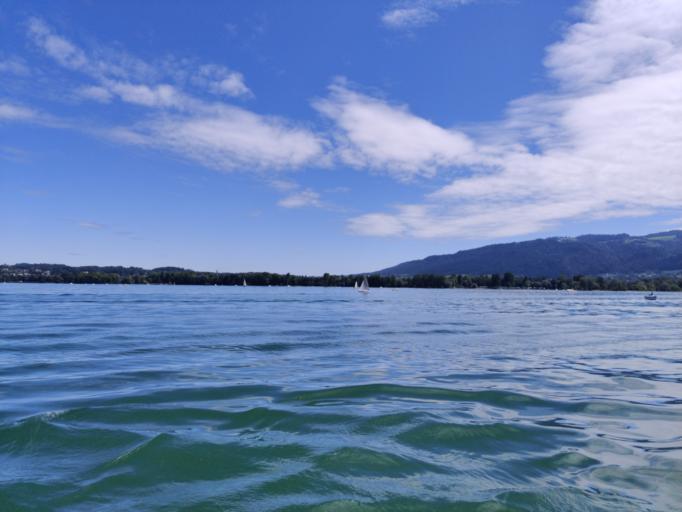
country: AT
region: Vorarlberg
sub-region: Politischer Bezirk Bregenz
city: Lochau
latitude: 47.5310
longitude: 9.7158
